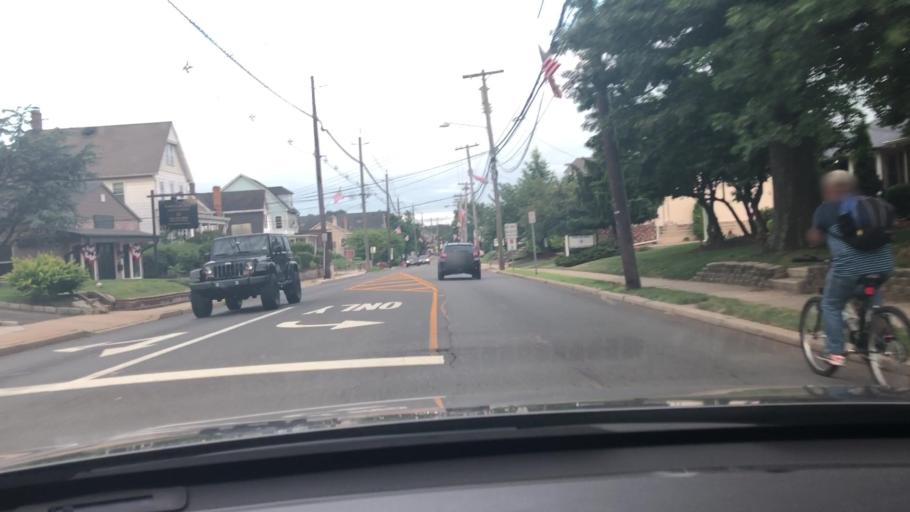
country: US
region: New Jersey
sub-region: Middlesex County
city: Milltown
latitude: 40.4558
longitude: -74.4437
